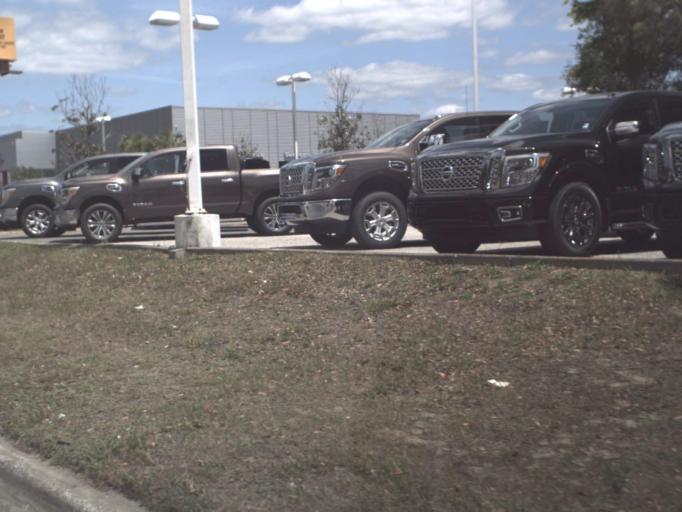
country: US
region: Florida
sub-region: Marion County
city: Ocala
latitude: 29.1720
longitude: -82.1612
